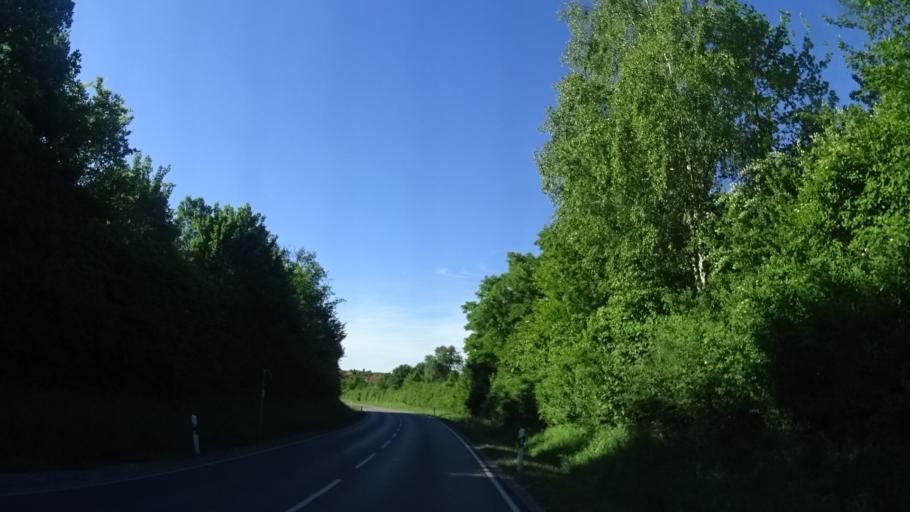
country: DE
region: Baden-Wuerttemberg
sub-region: Regierungsbezirk Stuttgart
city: Vellberg
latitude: 49.0785
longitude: 9.8717
